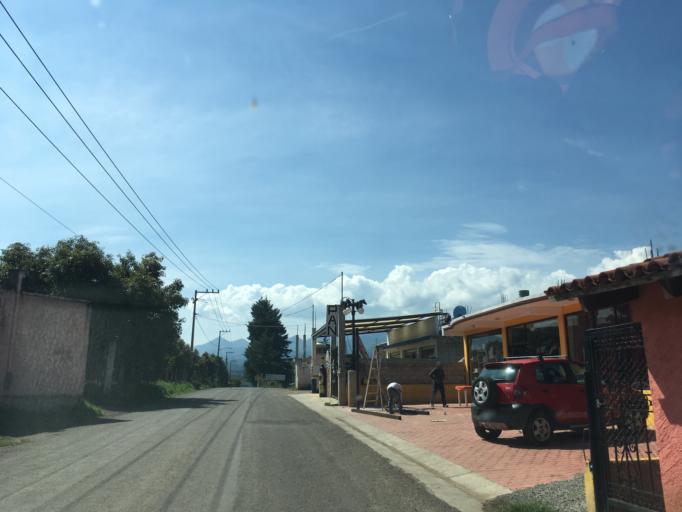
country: MX
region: Michoacan
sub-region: Zitacuaro
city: La Fundicion (Quinta Manzana)
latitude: 19.4868
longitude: -100.3172
